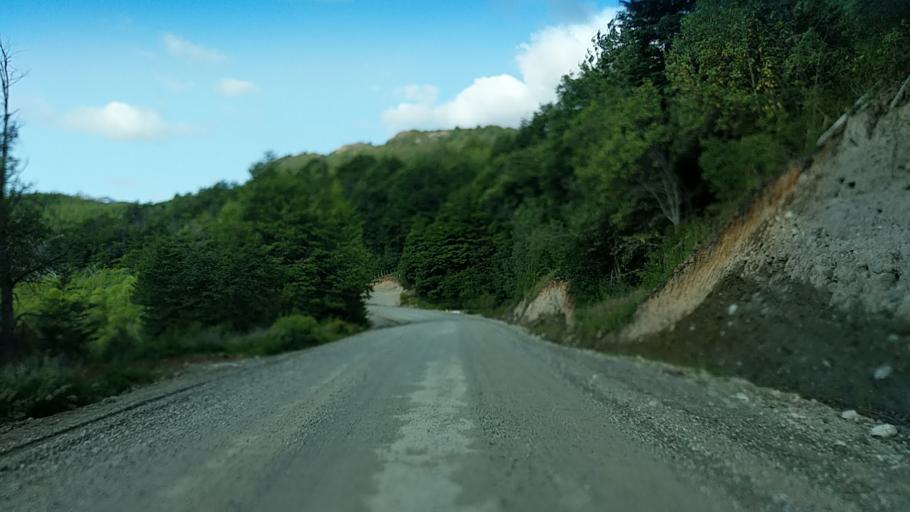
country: CL
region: Los Lagos
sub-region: Provincia de Palena
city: Futaleufu
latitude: -43.2391
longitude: -71.9263
